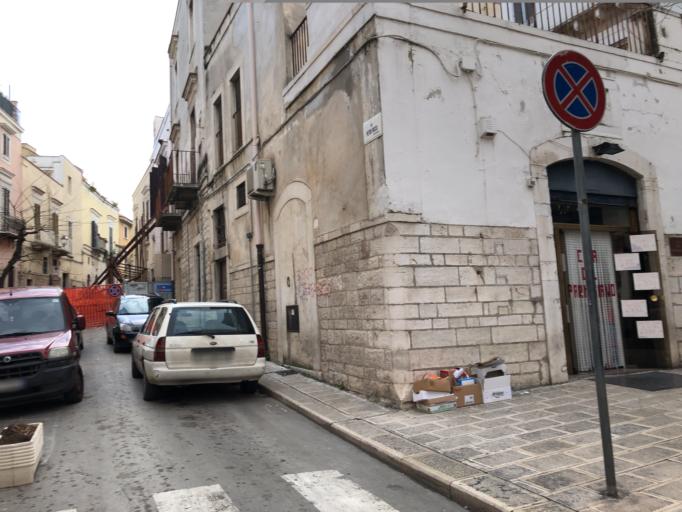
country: IT
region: Apulia
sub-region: Provincia di Barletta - Andria - Trani
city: Andria
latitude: 41.2264
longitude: 16.2976
